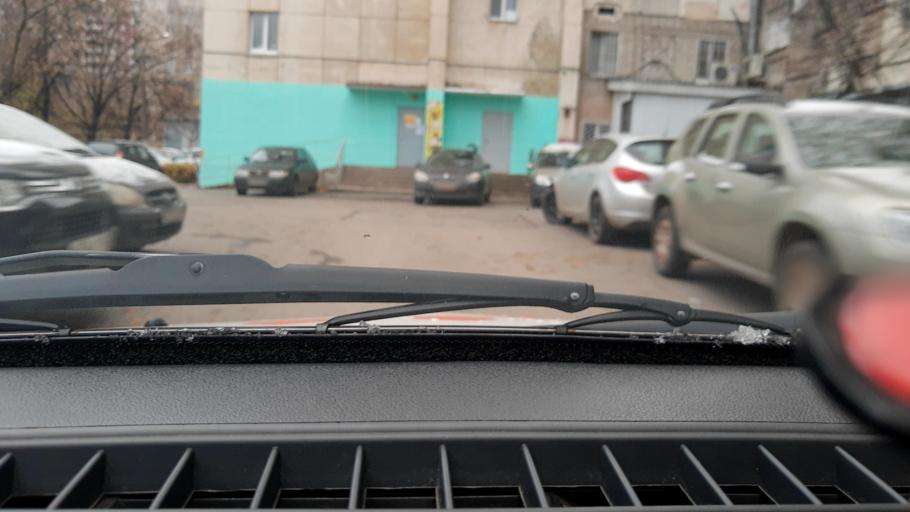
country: RU
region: Bashkortostan
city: Ufa
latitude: 54.7885
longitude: 56.0416
